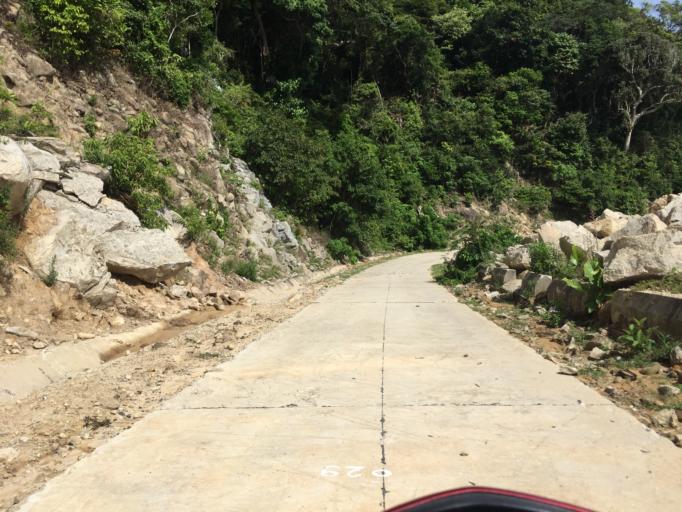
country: VN
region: Quang Nam
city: Hoi An
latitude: 15.9462
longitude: 108.5308
